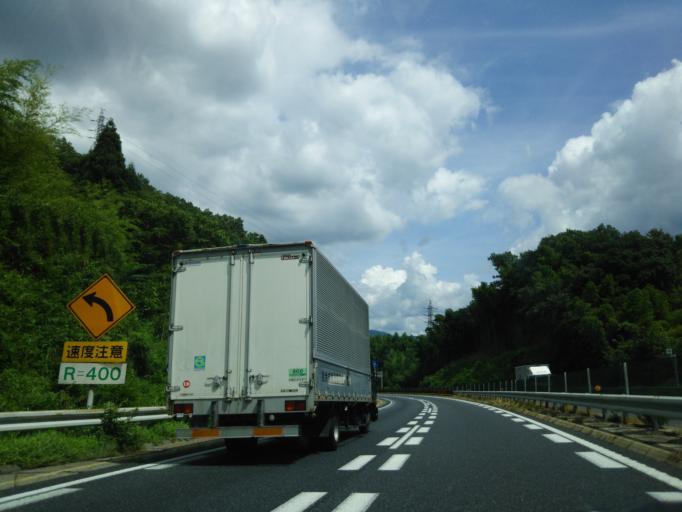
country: JP
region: Gifu
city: Mizunami
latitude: 35.3704
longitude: 137.2406
